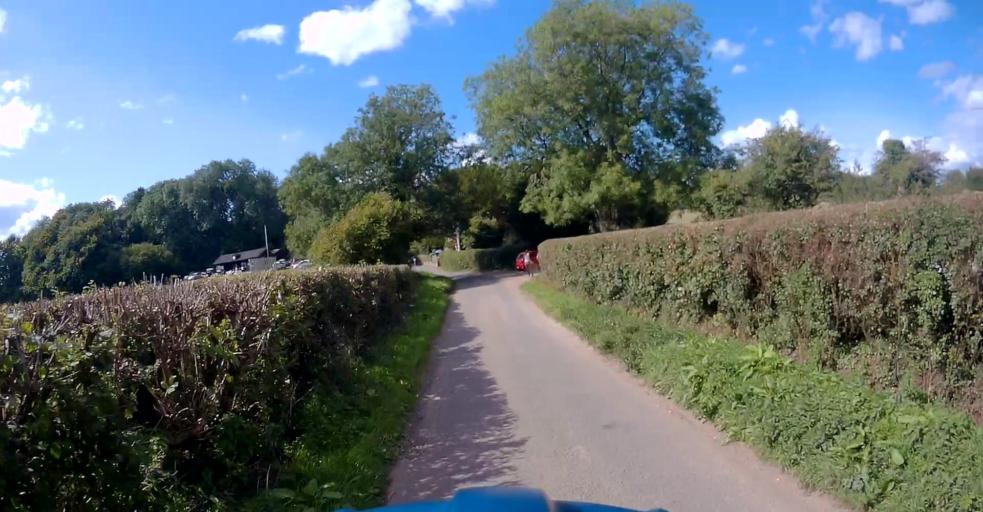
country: GB
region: England
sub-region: Hampshire
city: Four Marks
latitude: 51.1528
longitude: -1.0903
